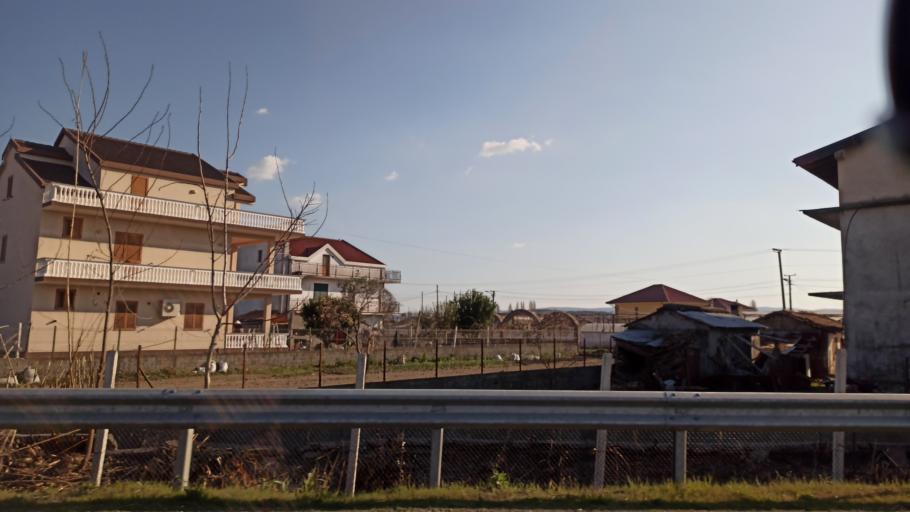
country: AL
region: Shkoder
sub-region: Rrethi i Shkodres
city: Vau i Dejes
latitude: 41.9900
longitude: 19.5828
